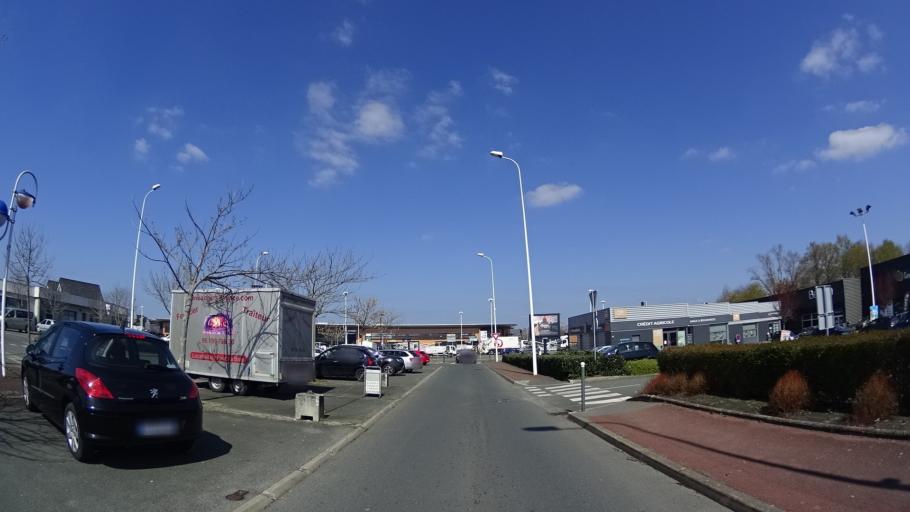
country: FR
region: Pays de la Loire
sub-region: Departement de Maine-et-Loire
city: Murs-Erigne
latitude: 47.3968
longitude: -0.5284
